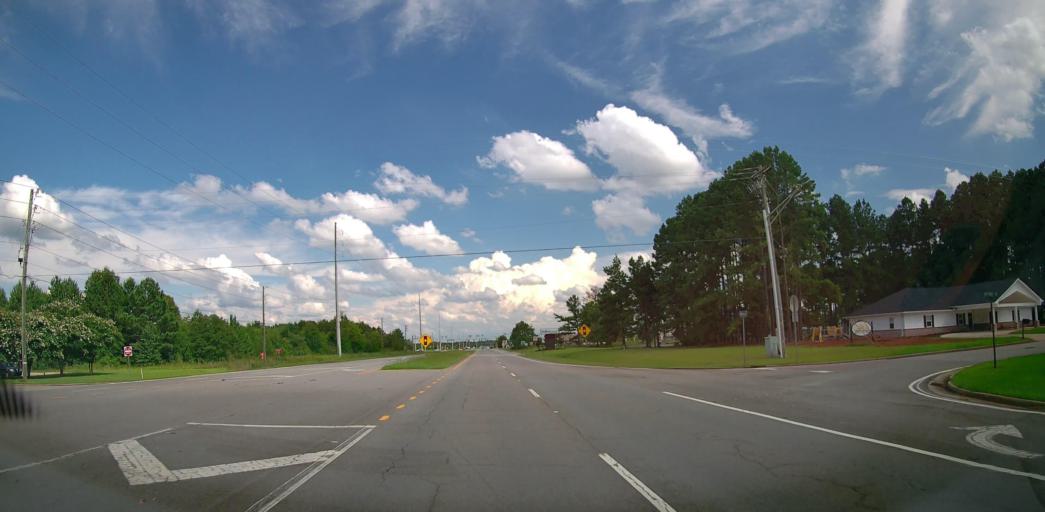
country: US
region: Georgia
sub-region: Houston County
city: Perry
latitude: 32.4776
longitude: -83.7079
